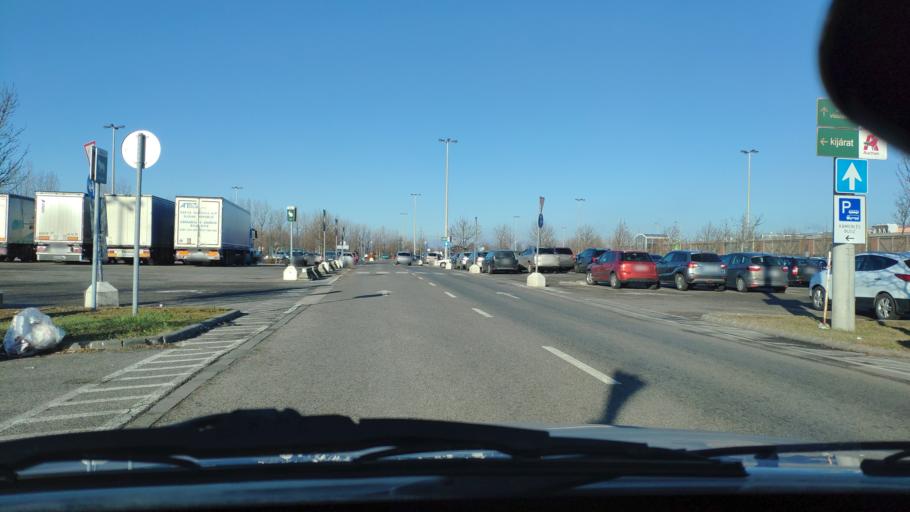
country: HU
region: Budapest
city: Budapest XVIII. keruelet
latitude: 47.4172
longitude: 19.1573
